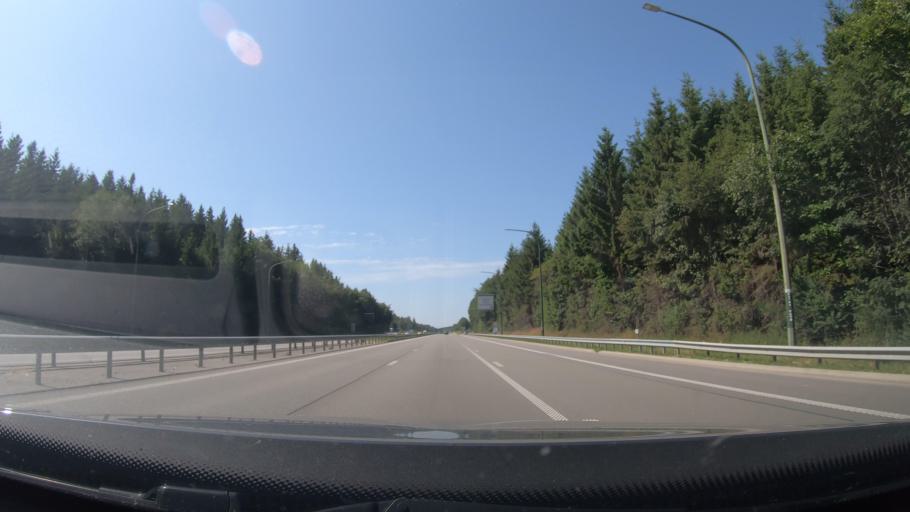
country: BE
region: Wallonia
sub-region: Province de Liege
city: Saint-Vith
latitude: 50.3225
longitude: 6.0877
